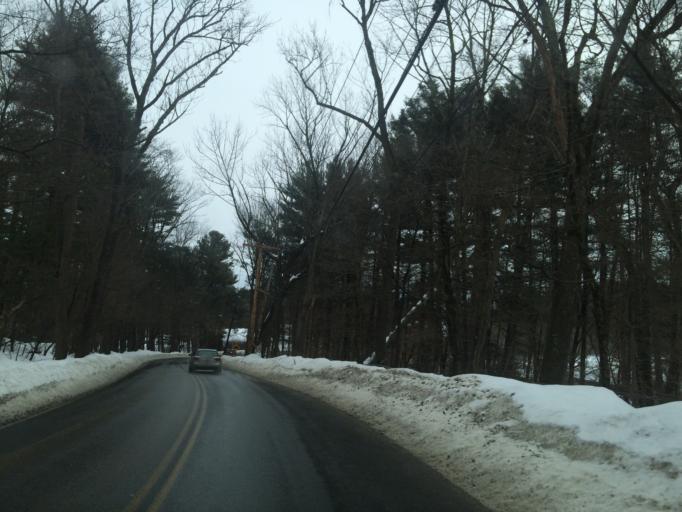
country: US
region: Massachusetts
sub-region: Middlesex County
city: Lincoln
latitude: 42.4086
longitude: -71.3272
